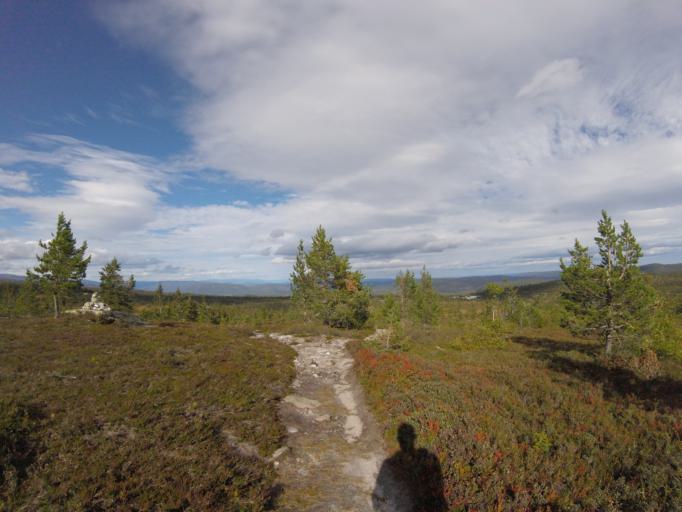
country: NO
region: Buskerud
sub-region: Flesberg
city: Lampeland
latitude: 59.7608
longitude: 9.4301
